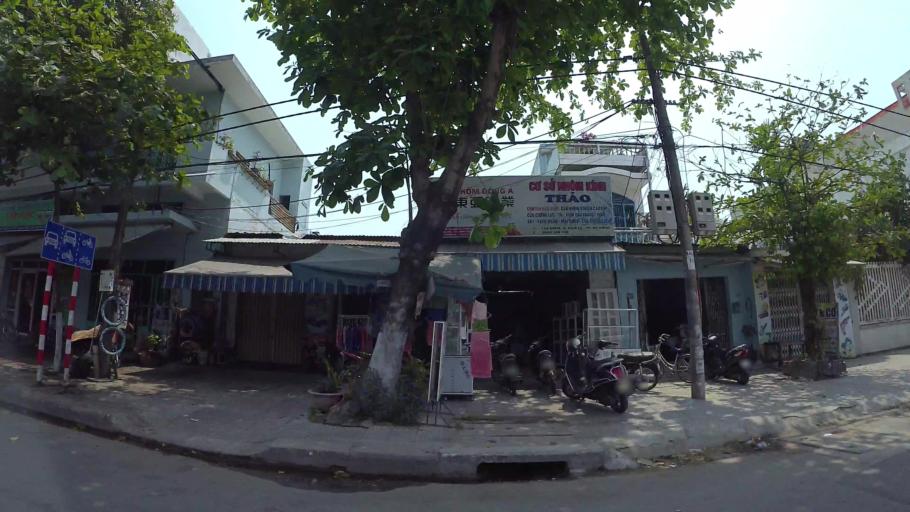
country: VN
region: Da Nang
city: Cam Le
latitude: 16.0207
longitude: 108.2119
